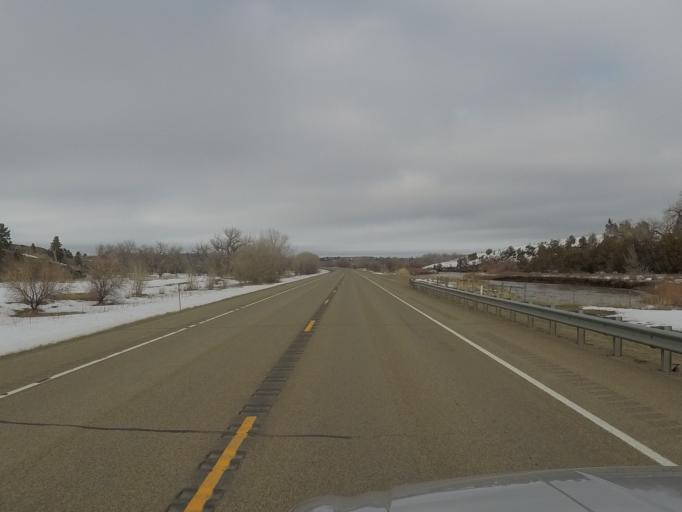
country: US
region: Montana
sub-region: Golden Valley County
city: Ryegate
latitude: 46.3060
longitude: -109.1993
